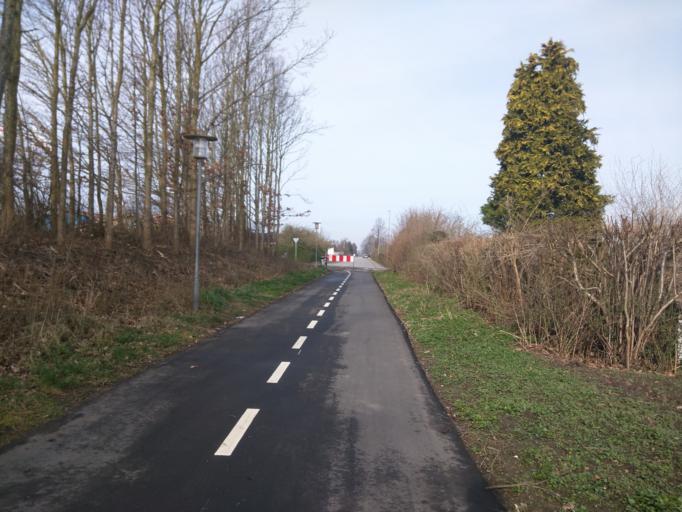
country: DK
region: South Denmark
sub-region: Fredericia Kommune
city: Snoghoj
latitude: 55.5446
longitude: 9.7047
